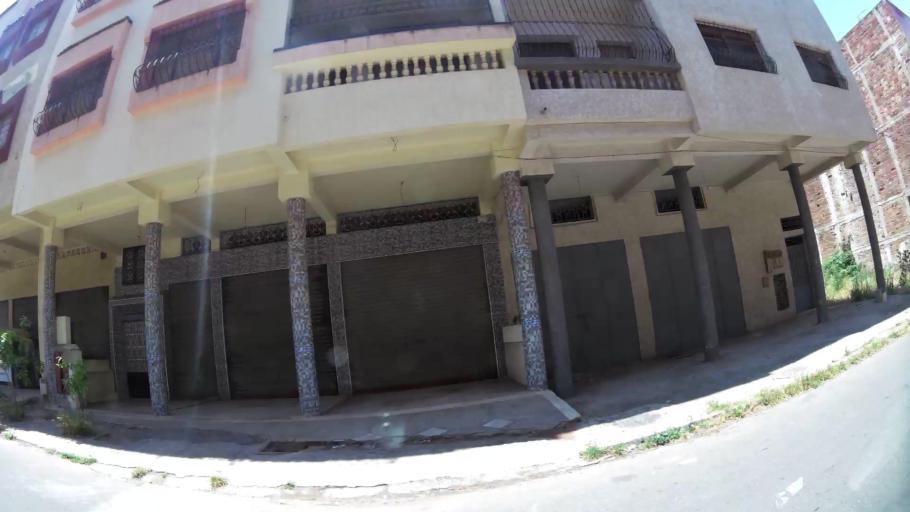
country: MA
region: Gharb-Chrarda-Beni Hssen
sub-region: Kenitra Province
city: Kenitra
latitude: 34.2544
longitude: -6.6211
